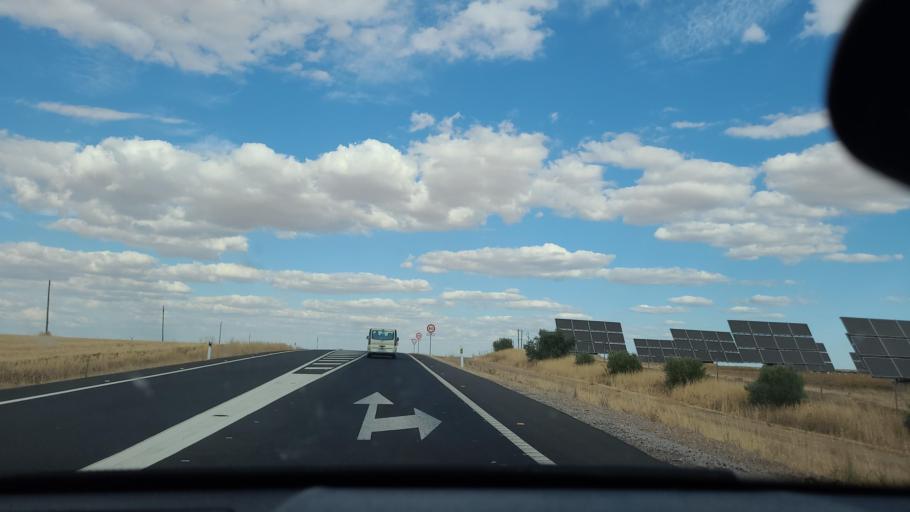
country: ES
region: Extremadura
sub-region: Provincia de Badajoz
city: Casas de Reina
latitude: 38.2468
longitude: -5.9646
